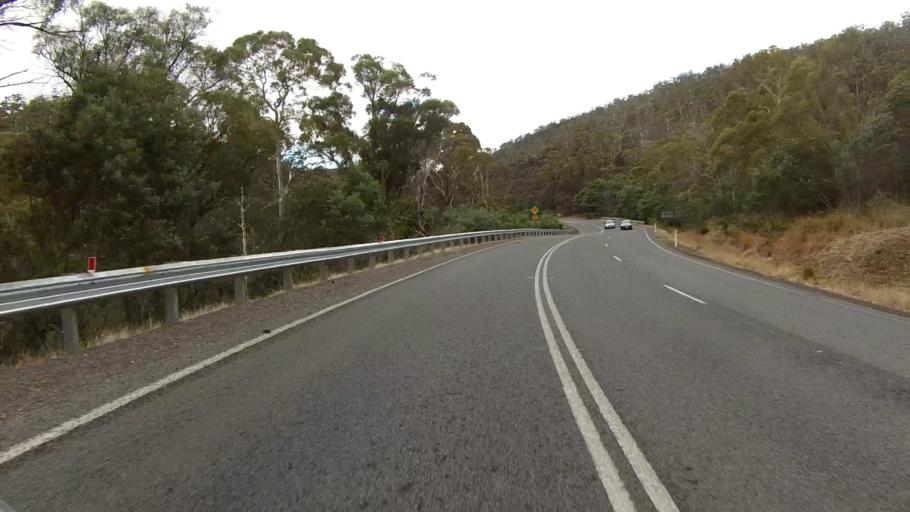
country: AU
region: Tasmania
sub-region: Sorell
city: Sorell
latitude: -42.5704
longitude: 147.8215
